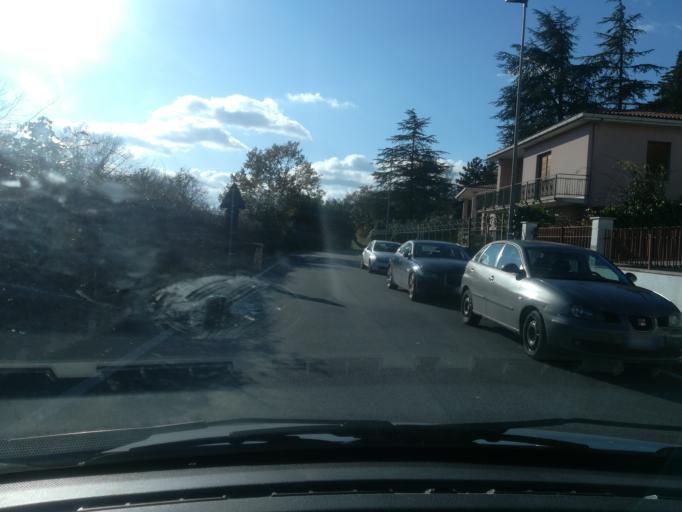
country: IT
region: The Marches
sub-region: Provincia di Macerata
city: Macerata
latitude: 43.2911
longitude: 13.4399
